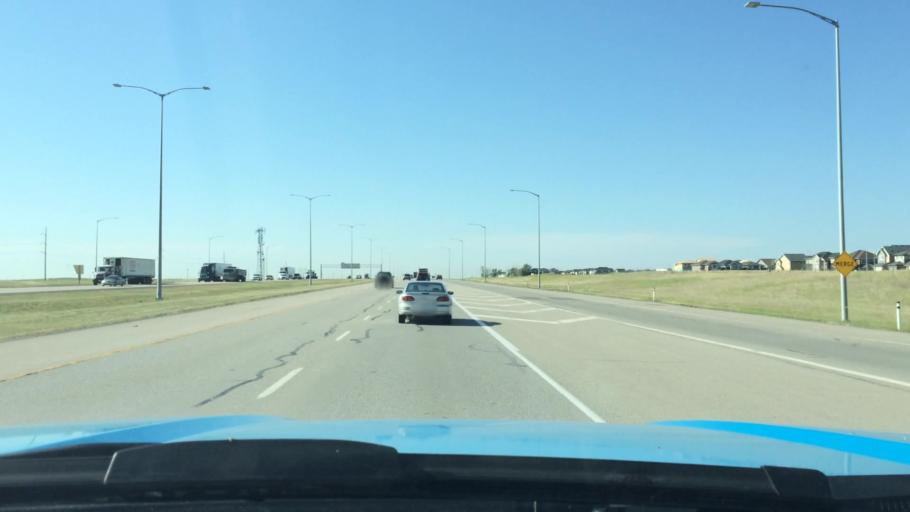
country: CA
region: Alberta
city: Chestermere
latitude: 51.1325
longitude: -113.9216
